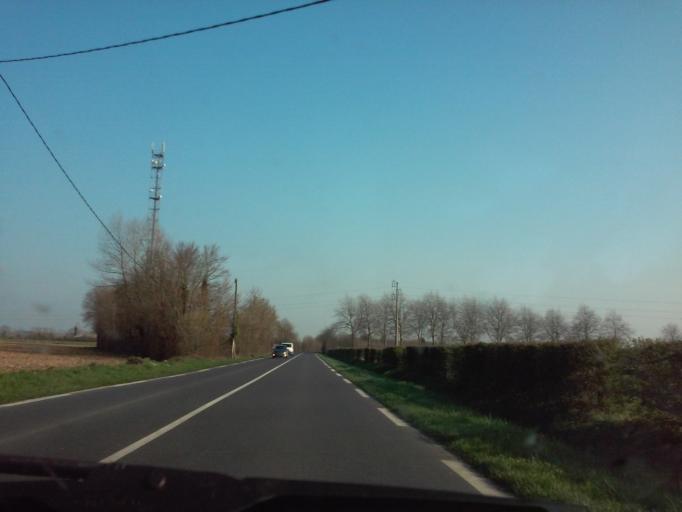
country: FR
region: Lower Normandy
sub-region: Departement du Calvados
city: Saint-Vigor-le-Grand
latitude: 49.2465
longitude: -0.6786
